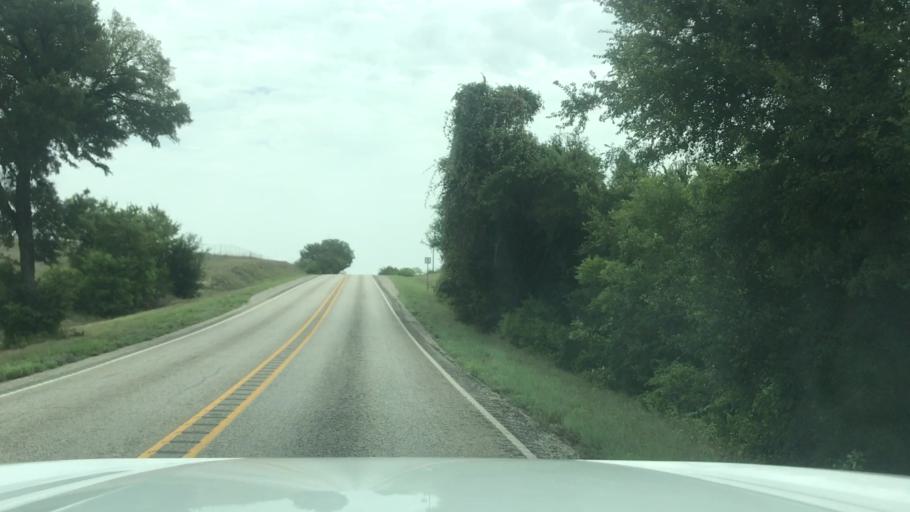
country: US
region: Texas
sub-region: Hamilton County
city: Hico
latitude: 32.0550
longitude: -98.1785
